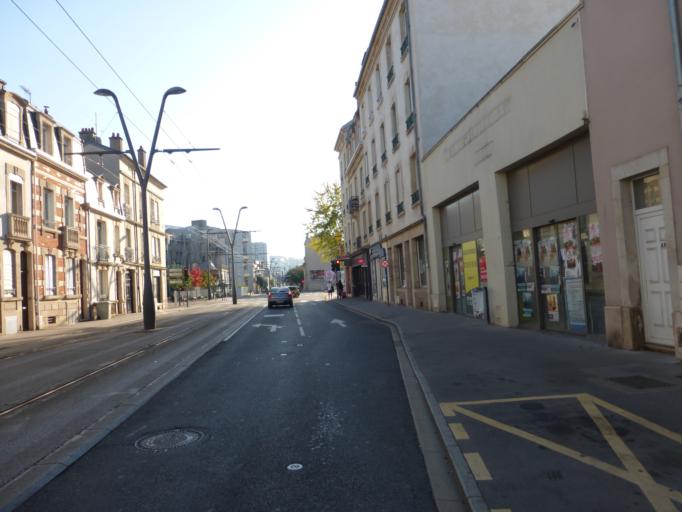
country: FR
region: Lorraine
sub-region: Departement de Meurthe-et-Moselle
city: Nancy
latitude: 48.6727
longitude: 6.1732
